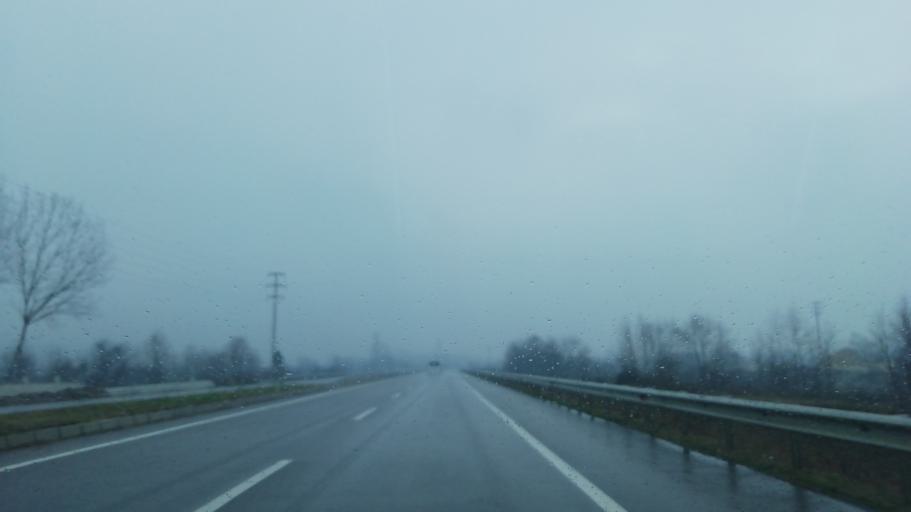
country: TR
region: Sakarya
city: Akyazi
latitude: 40.6478
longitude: 30.6073
